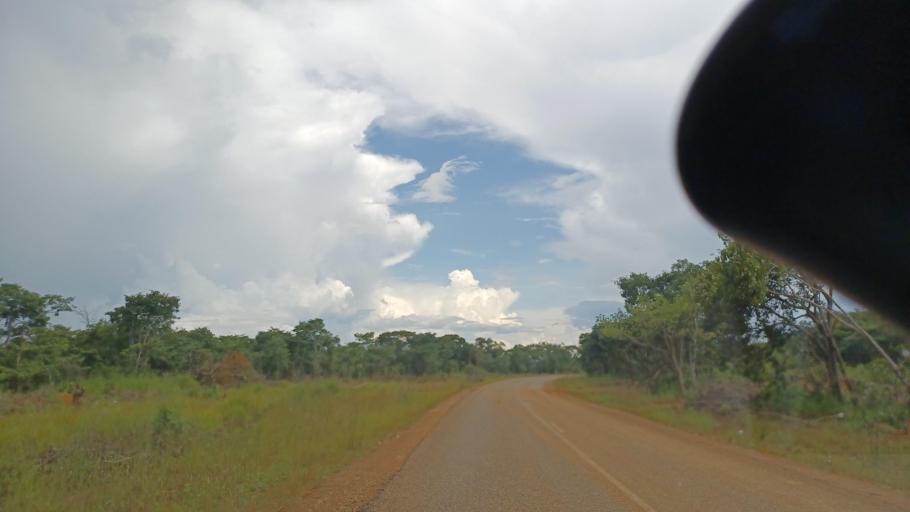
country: ZM
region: North-Western
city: Kasempa
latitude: -13.1304
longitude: 25.8757
